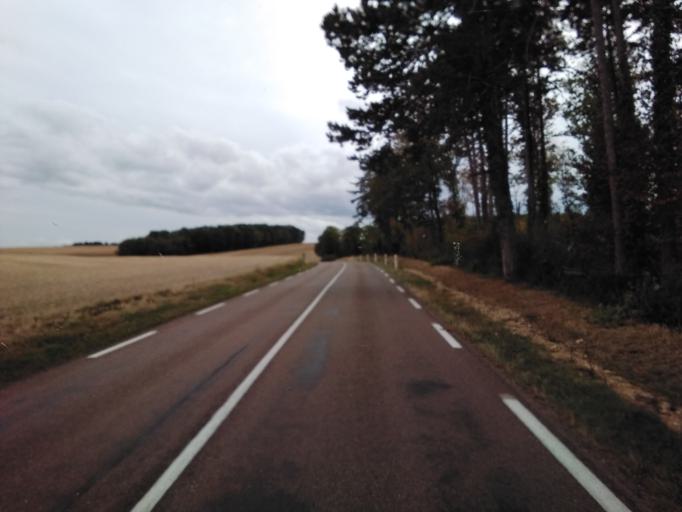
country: FR
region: Champagne-Ardenne
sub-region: Departement de l'Aube
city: Bar-sur-Seine
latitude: 48.1544
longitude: 4.4103
